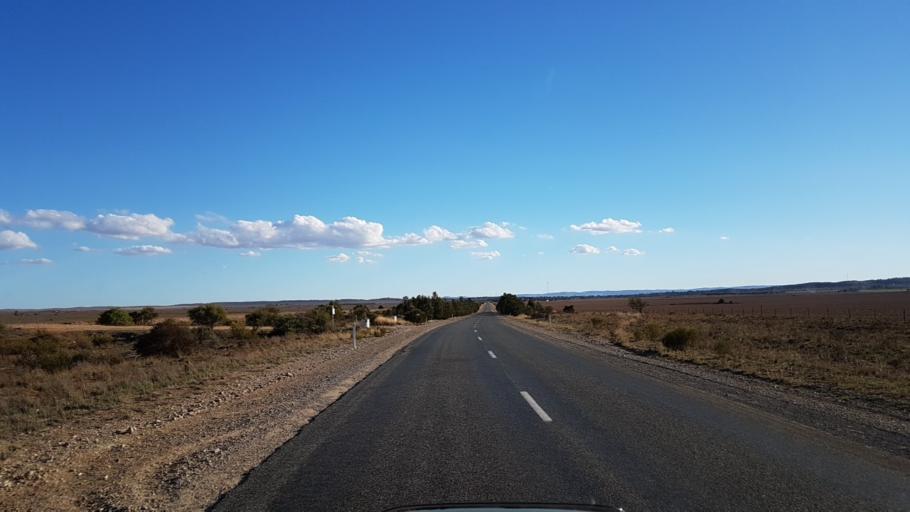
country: AU
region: South Australia
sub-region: Peterborough
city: Peterborough
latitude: -32.9613
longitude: 138.8889
